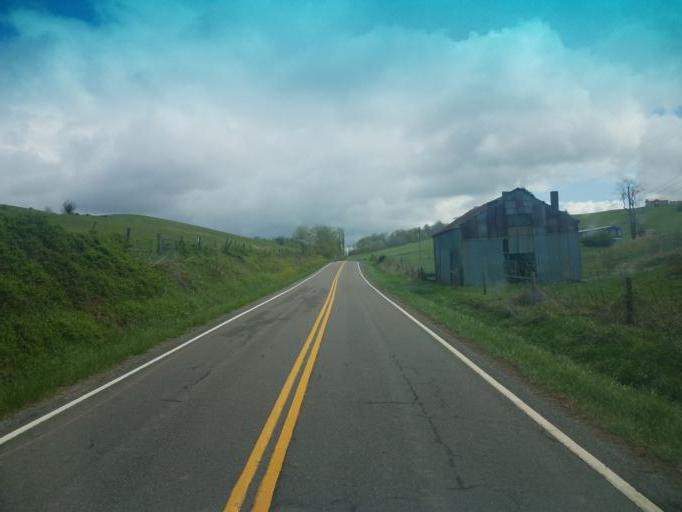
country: US
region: Virginia
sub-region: Smyth County
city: Atkins
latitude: 37.0017
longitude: -81.3736
